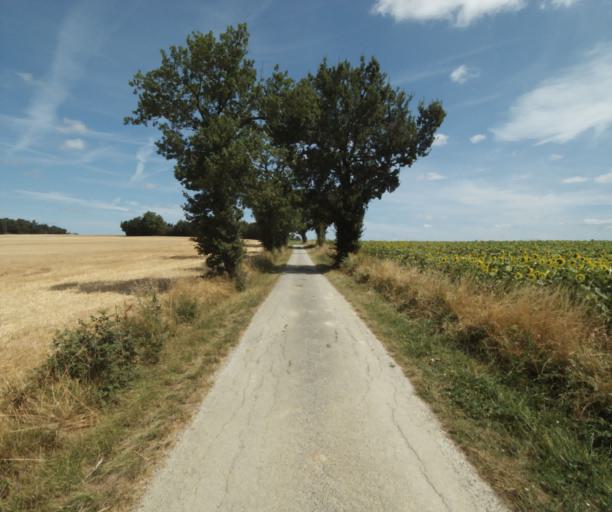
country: FR
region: Midi-Pyrenees
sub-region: Departement du Tarn
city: Soreze
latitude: 43.4858
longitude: 2.0700
